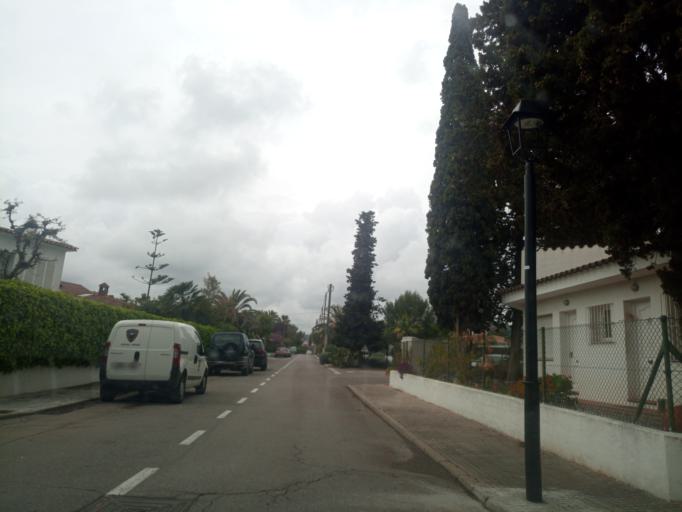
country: ES
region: Catalonia
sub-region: Provincia de Barcelona
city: Sant Pere de Ribes
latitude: 41.2530
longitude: 1.7794
